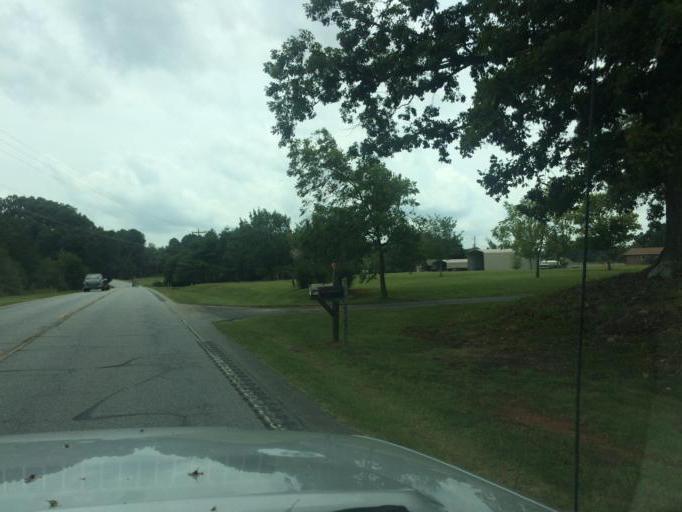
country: US
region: South Carolina
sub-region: Anderson County
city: Centerville
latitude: 34.4680
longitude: -82.7871
